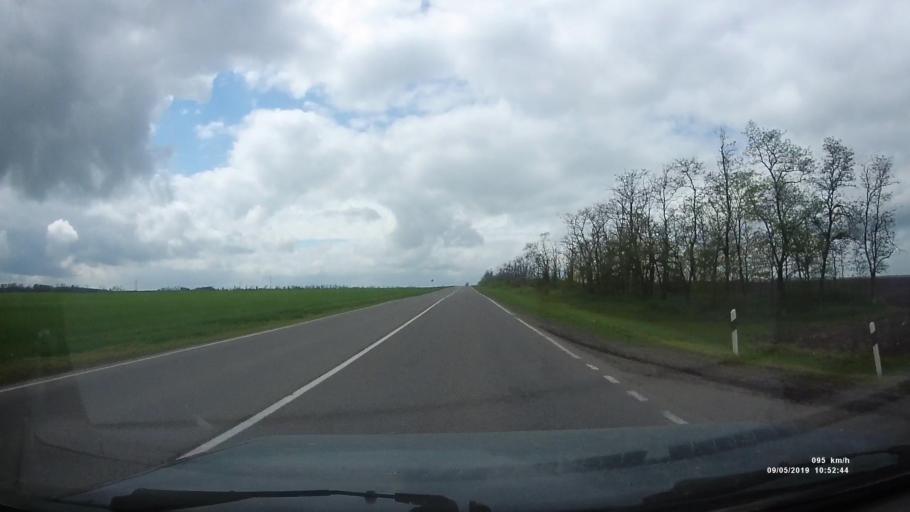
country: RU
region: Rostov
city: Peshkovo
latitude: 46.8971
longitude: 39.3500
